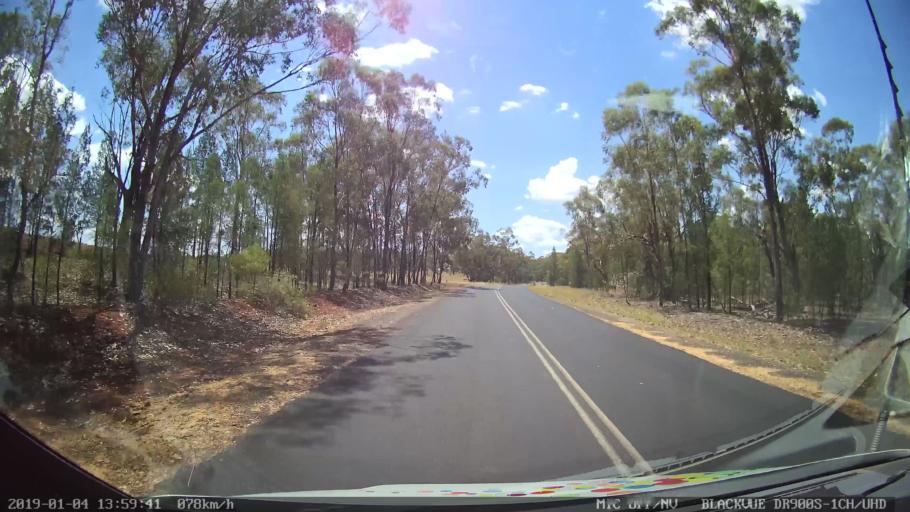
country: AU
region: New South Wales
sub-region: Dubbo Municipality
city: Dubbo
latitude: -32.3141
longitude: 148.5888
